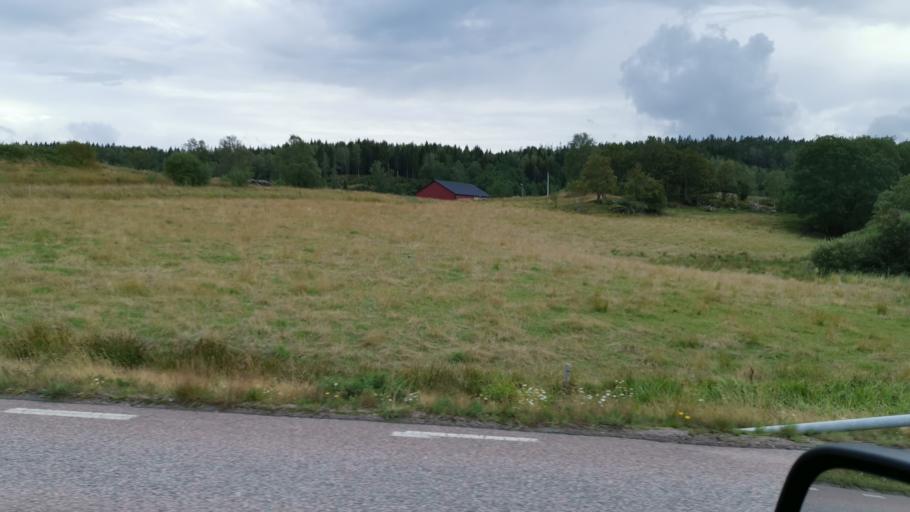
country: SE
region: Vaestra Goetaland
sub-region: Munkedals Kommun
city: Munkedal
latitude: 58.3918
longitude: 11.7546
